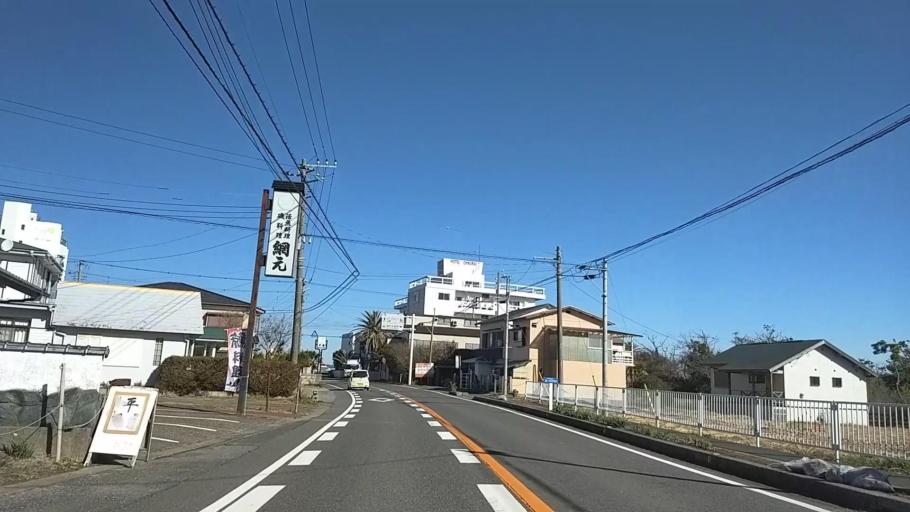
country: JP
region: Chiba
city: Tateyama
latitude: 34.9777
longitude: 139.9656
